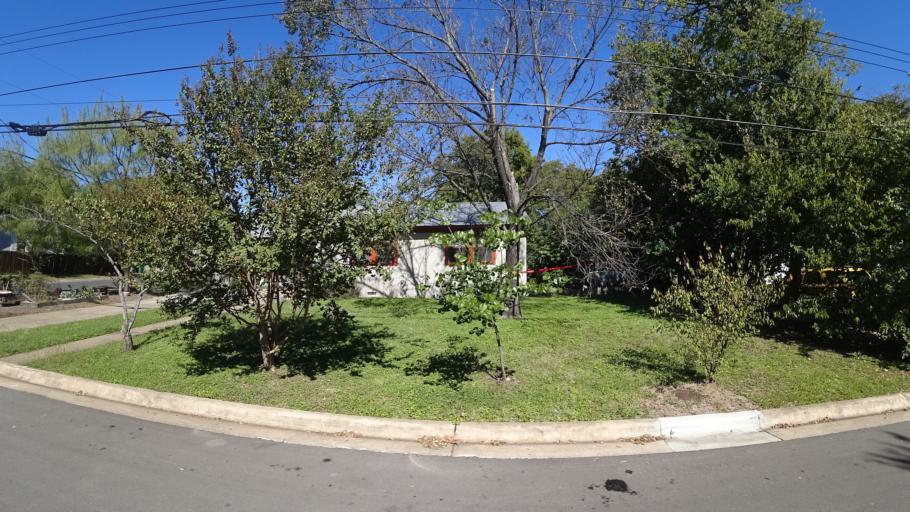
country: US
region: Texas
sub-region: Travis County
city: Austin
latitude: 30.3348
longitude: -97.7359
